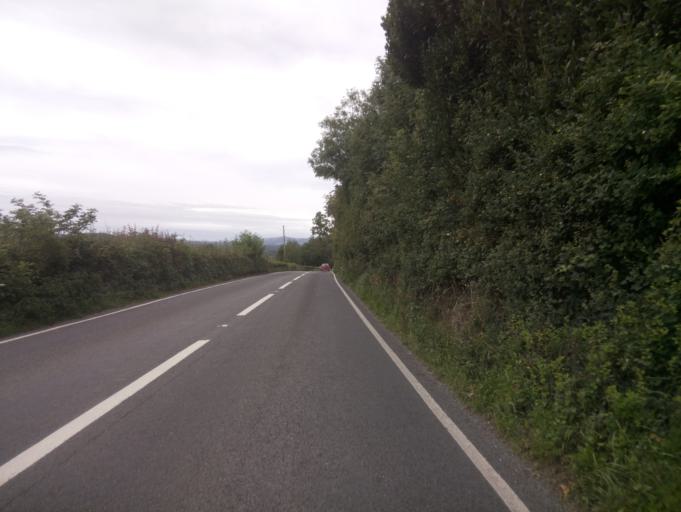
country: GB
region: England
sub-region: Somerset
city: Bradley Cross
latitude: 51.2444
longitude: -2.7337
